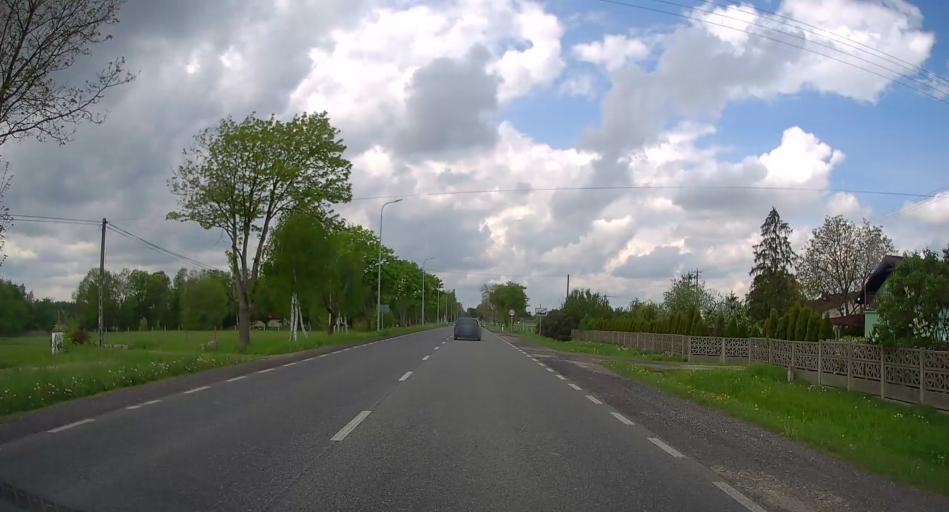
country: PL
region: Masovian Voivodeship
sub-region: Powiat plonski
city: Zaluski
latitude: 52.4457
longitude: 20.5119
